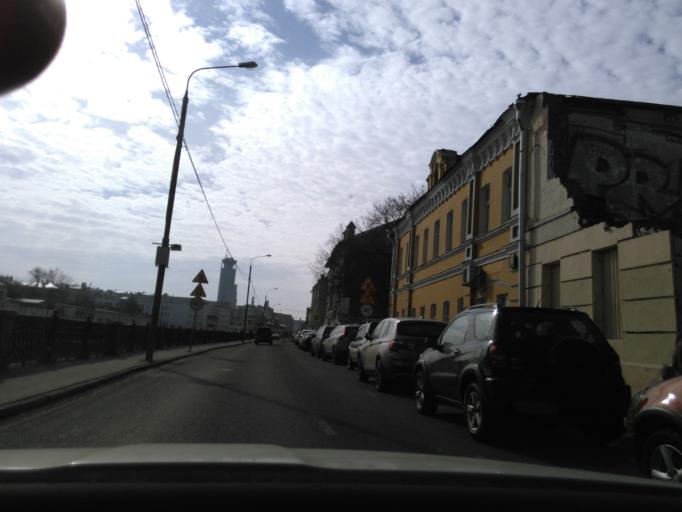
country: RU
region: Moscow
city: Zamoskvorech'ye
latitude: 55.7423
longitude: 37.6369
